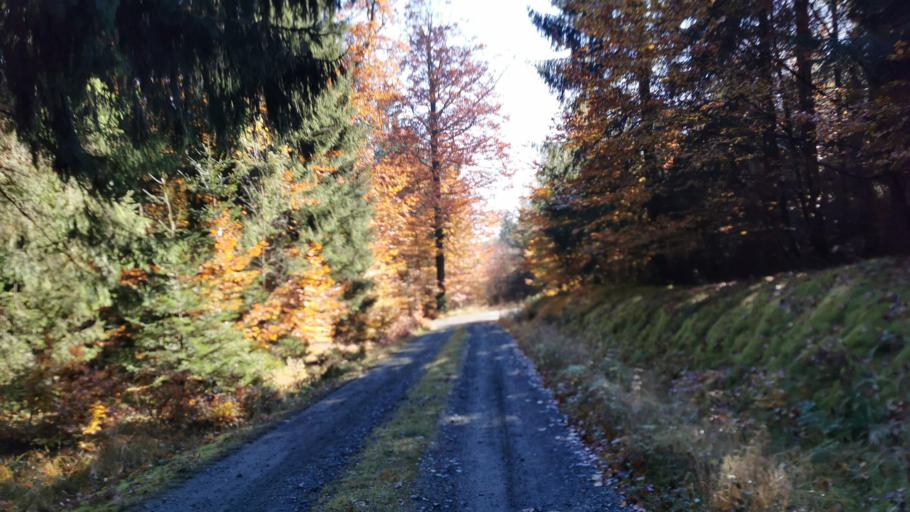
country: DE
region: Thuringia
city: Wurzbach
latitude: 50.4241
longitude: 11.5242
